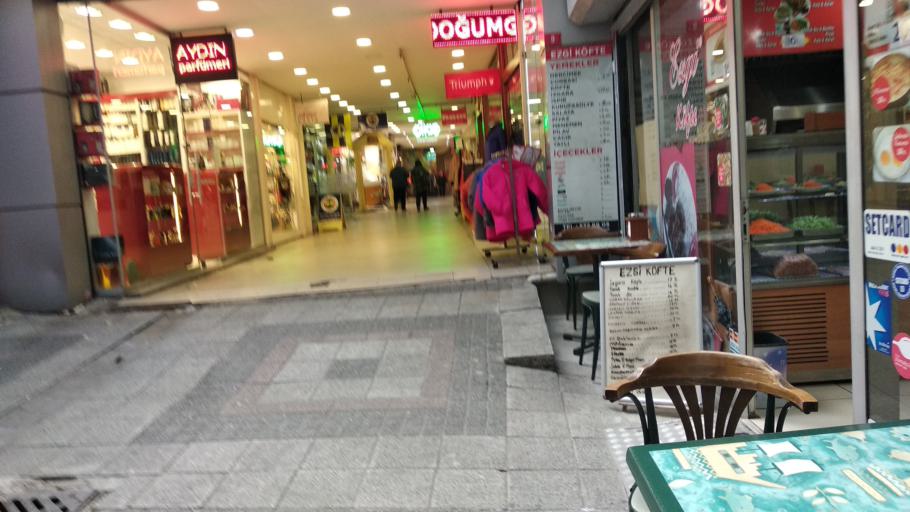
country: TR
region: Istanbul
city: Bahcelievler
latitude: 40.9789
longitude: 28.8743
